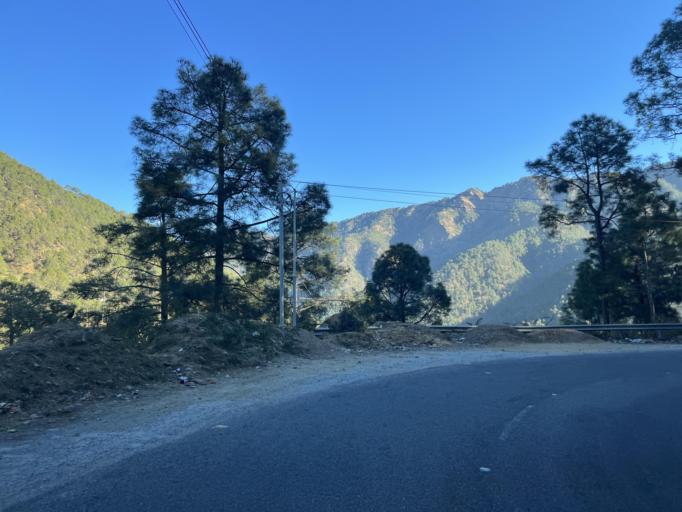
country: IN
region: Uttarakhand
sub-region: Naini Tal
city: Bhowali
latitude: 29.4049
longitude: 79.5103
